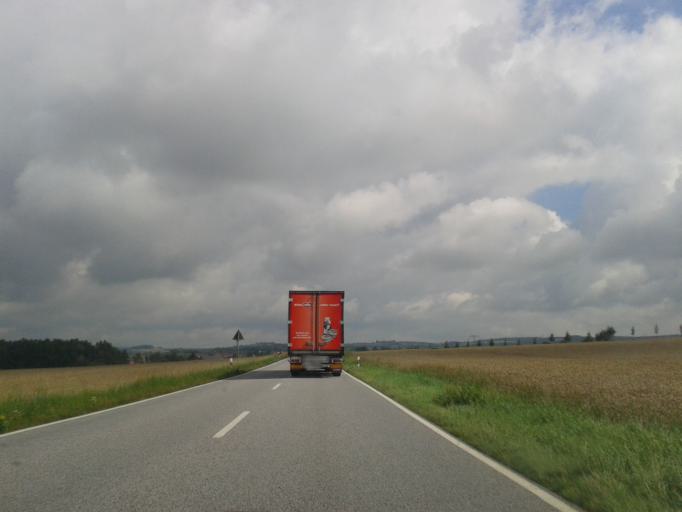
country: DE
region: Saxony
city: Lichtenberg
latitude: 51.1390
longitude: 13.9517
